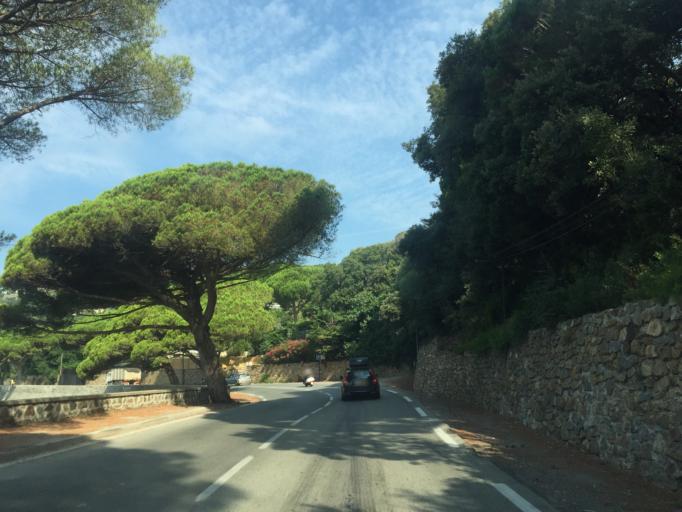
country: FR
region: Provence-Alpes-Cote d'Azur
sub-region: Departement du Var
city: Sainte-Maxime
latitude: 43.3141
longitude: 6.6624
